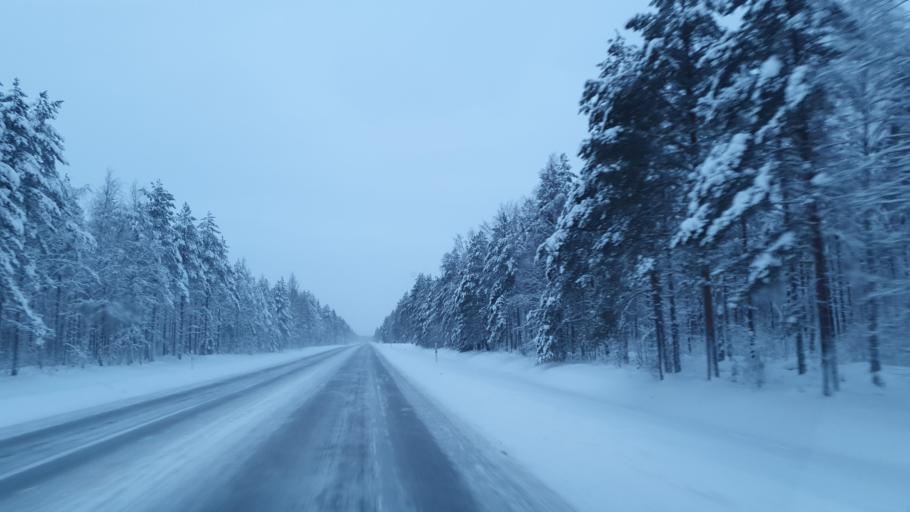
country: FI
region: Kainuu
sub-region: Kajaani
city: Vaala
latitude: 64.5976
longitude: 26.7283
